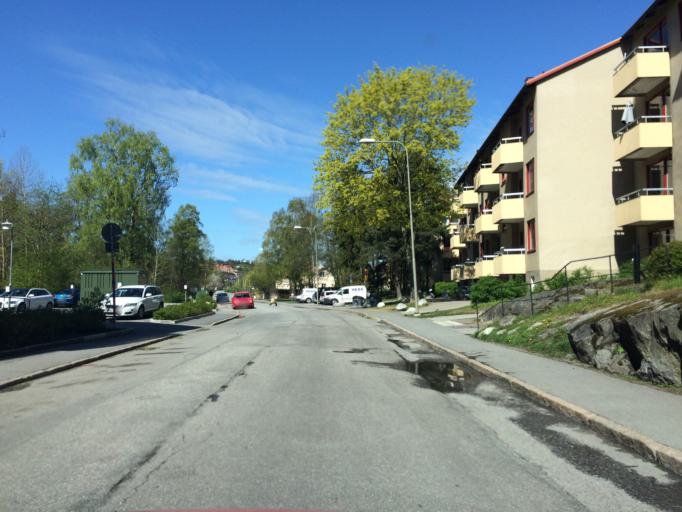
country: SE
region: Stockholm
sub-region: Huddinge Kommun
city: Segeltorp
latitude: 59.2942
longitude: 17.9653
